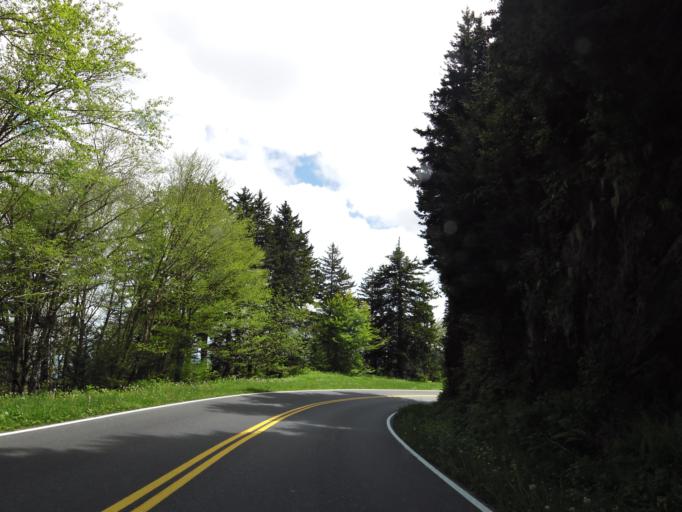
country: US
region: Tennessee
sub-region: Sevier County
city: Gatlinburg
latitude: 35.5802
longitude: -83.4781
